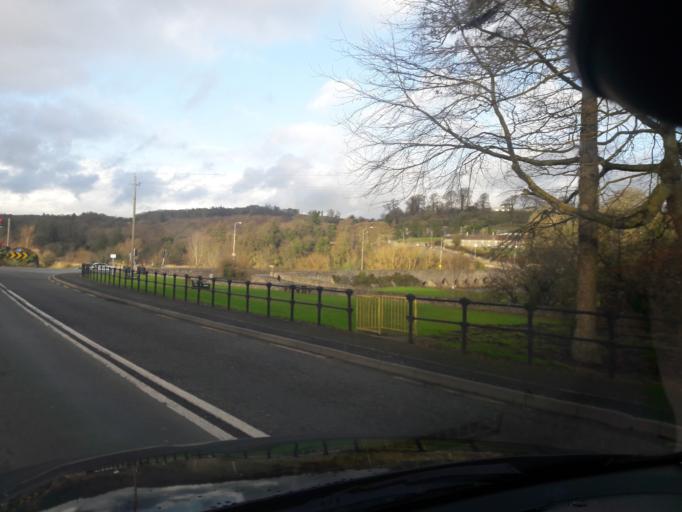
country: IE
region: Leinster
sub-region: An Mhi
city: Slane
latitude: 53.7021
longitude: -6.5413
